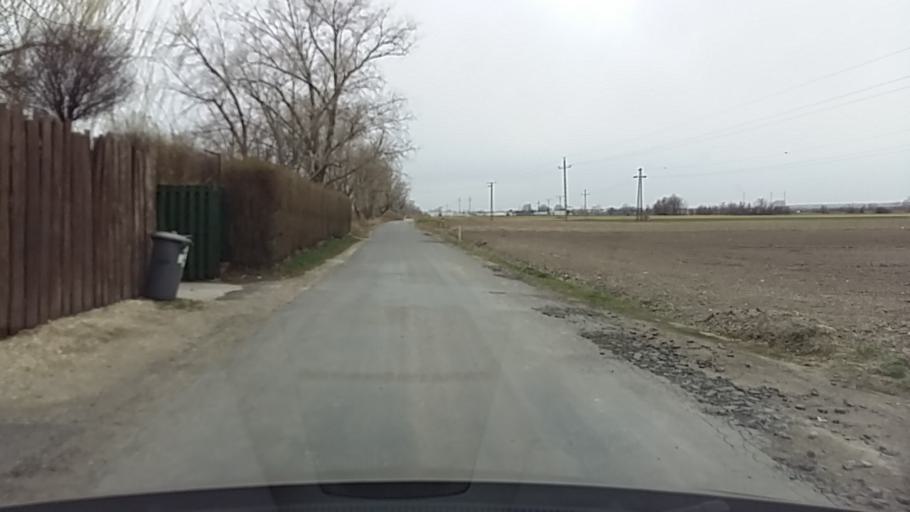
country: HU
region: Pest
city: Szigetszentmiklos
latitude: 47.3488
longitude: 19.0155
